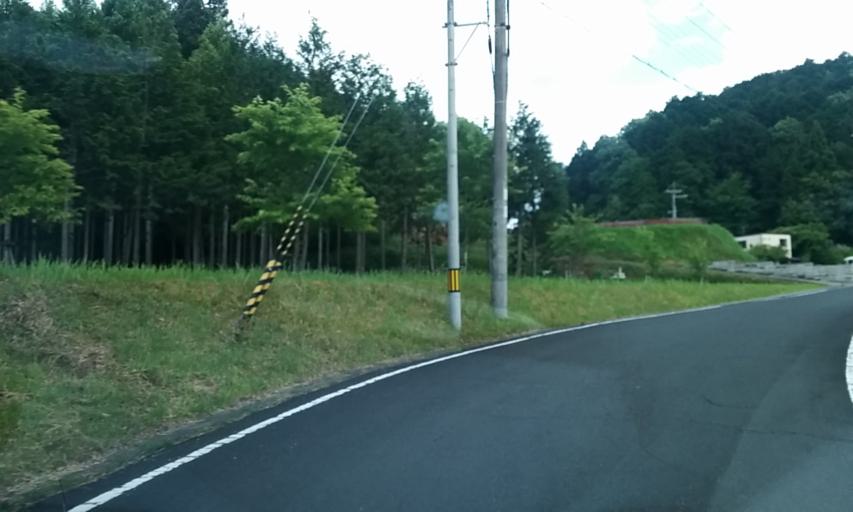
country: JP
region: Kyoto
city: Ayabe
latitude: 35.3671
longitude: 135.2436
